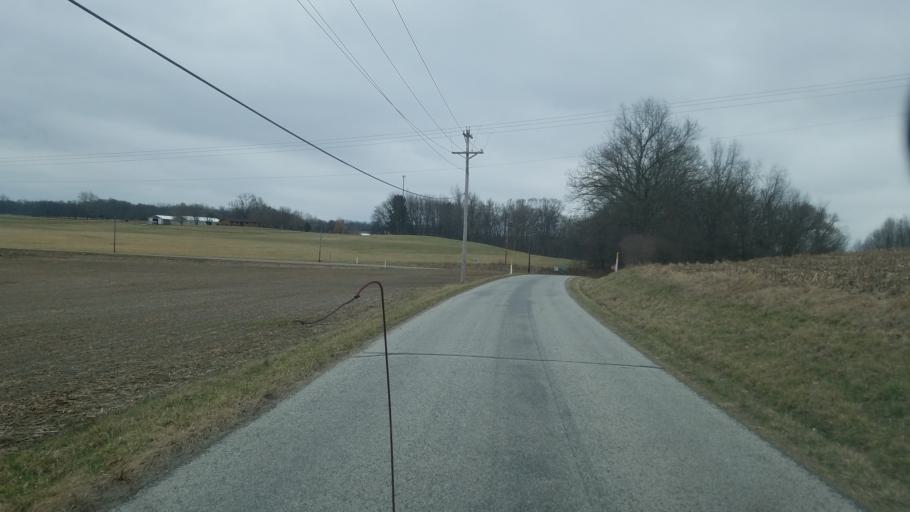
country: US
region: Ohio
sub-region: Licking County
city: Utica
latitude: 40.1912
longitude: -82.4006
